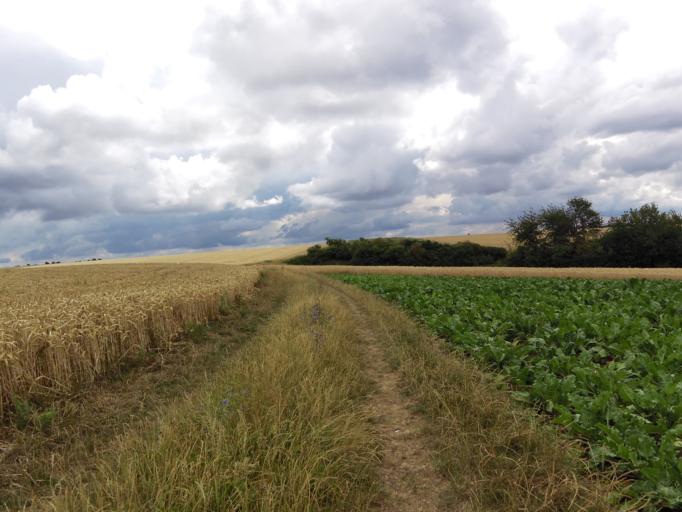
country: DE
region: Bavaria
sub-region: Regierungsbezirk Unterfranken
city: Estenfeld
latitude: 49.8202
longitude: 9.9747
